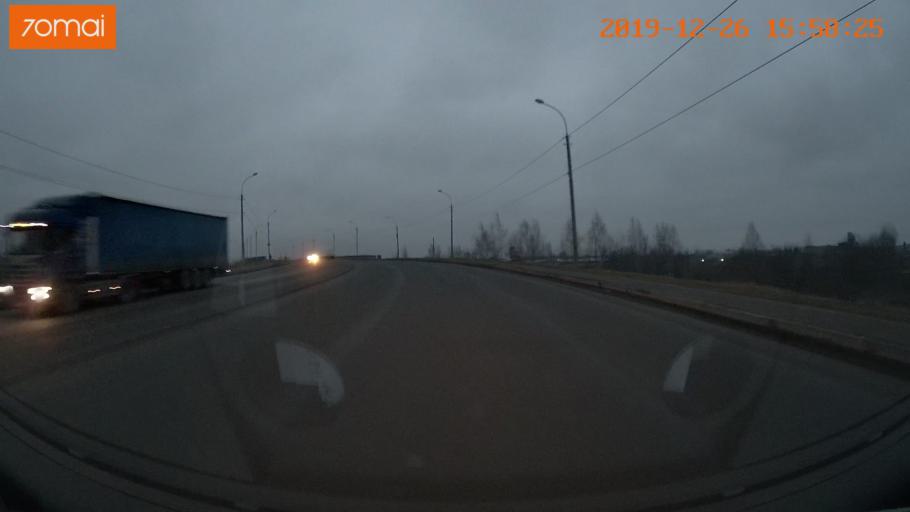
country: RU
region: Jaroslavl
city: Rybinsk
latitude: 58.0391
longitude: 38.7955
